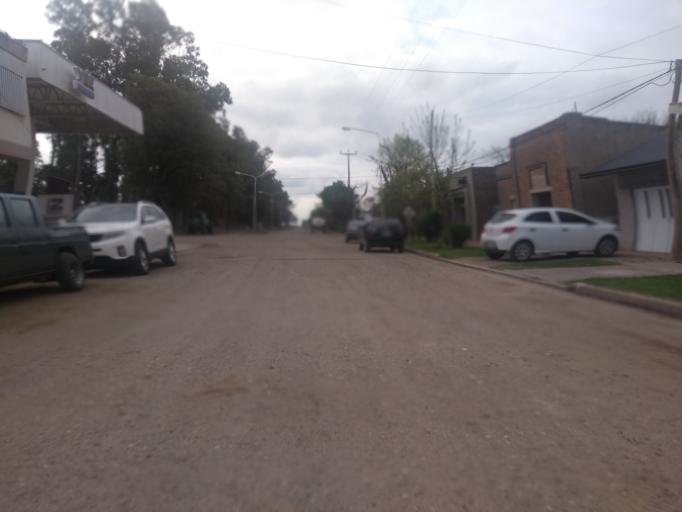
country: AR
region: Santa Fe
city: Galvez
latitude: -31.9076
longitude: -61.2800
